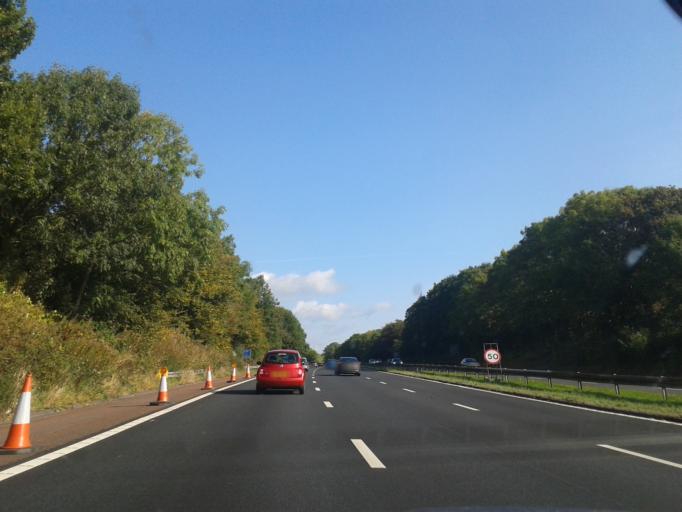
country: GB
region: England
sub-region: Lancashire
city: Bolton le Sands
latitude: 54.0806
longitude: -2.7704
